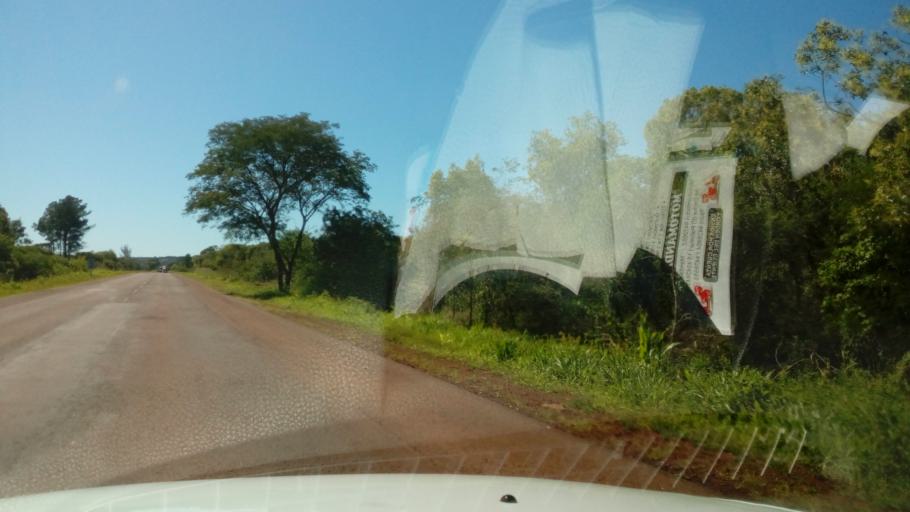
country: AR
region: Misiones
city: Almafuerte
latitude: -27.5685
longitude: -55.3972
